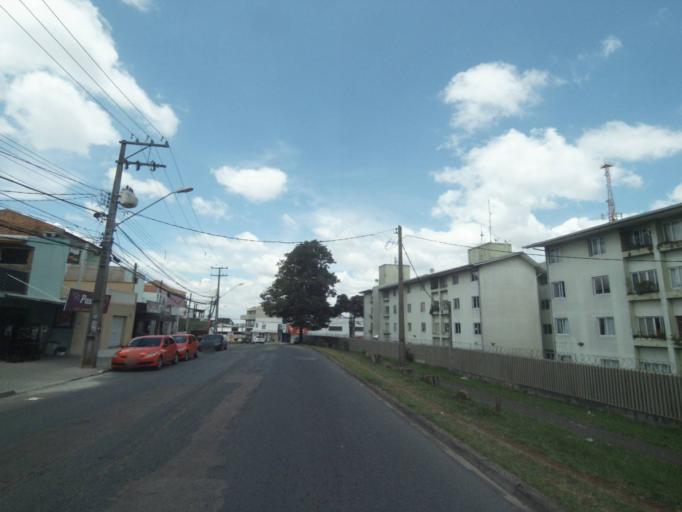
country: BR
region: Parana
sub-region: Curitiba
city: Curitiba
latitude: -25.4618
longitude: -49.3456
